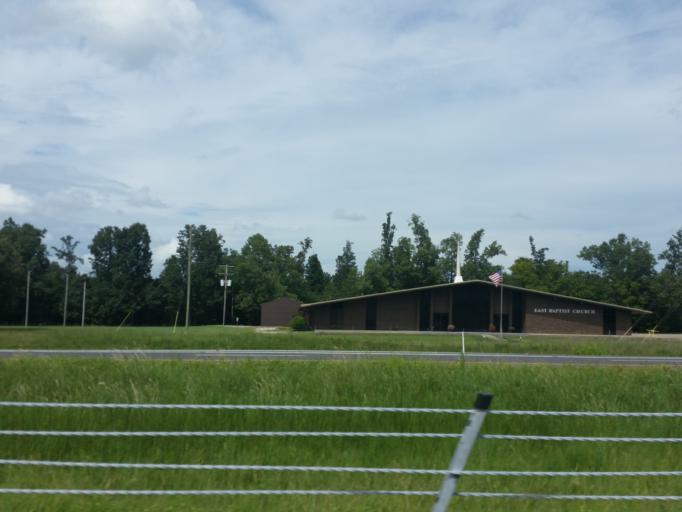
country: US
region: Kentucky
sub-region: McCracken County
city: Hendron
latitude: 37.0160
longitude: -88.5966
